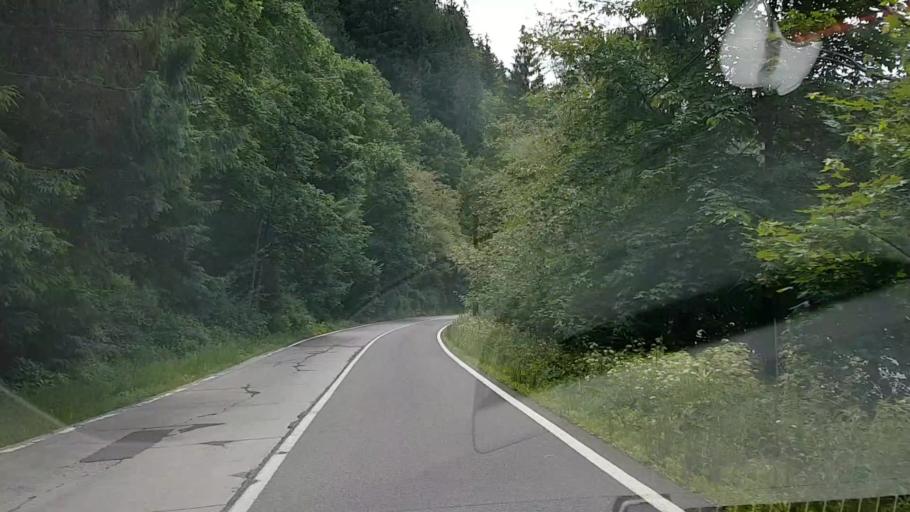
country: RO
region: Suceava
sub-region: Comuna Crucea
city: Crucea
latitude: 47.3786
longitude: 25.5878
